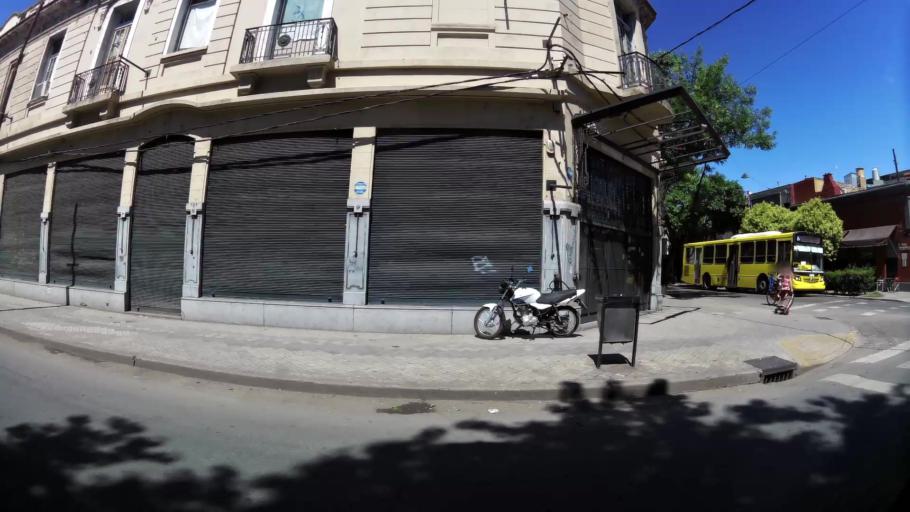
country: AR
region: Santa Fe
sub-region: Departamento de Rosario
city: Rosario
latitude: -32.9370
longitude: -60.6700
